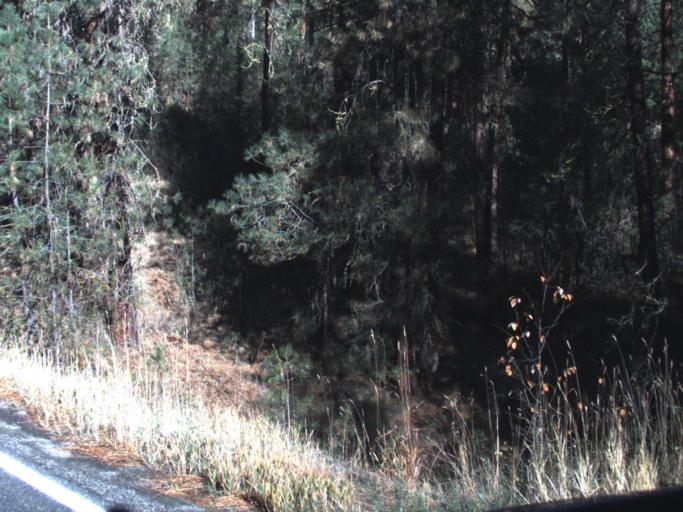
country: US
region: Washington
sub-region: Stevens County
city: Kettle Falls
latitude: 48.1932
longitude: -118.1713
